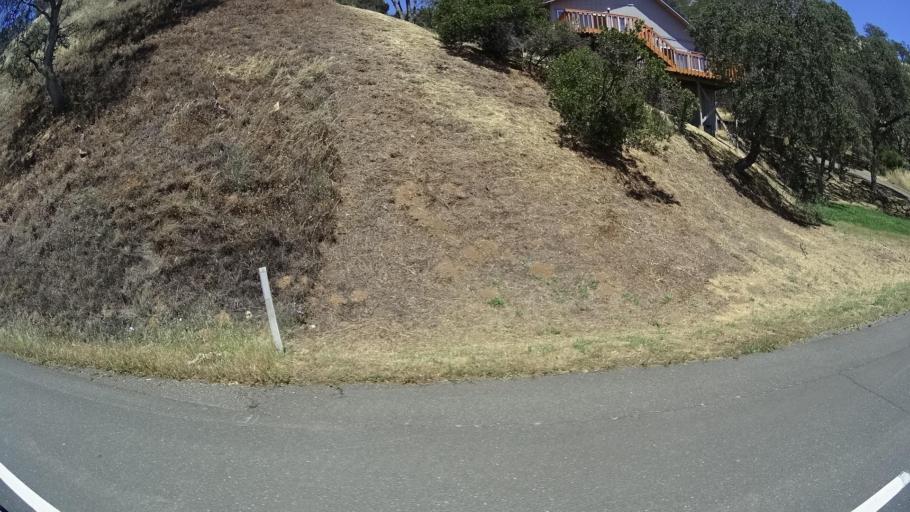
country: US
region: California
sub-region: Lake County
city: Soda Bay
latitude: 39.0410
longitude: -122.7732
